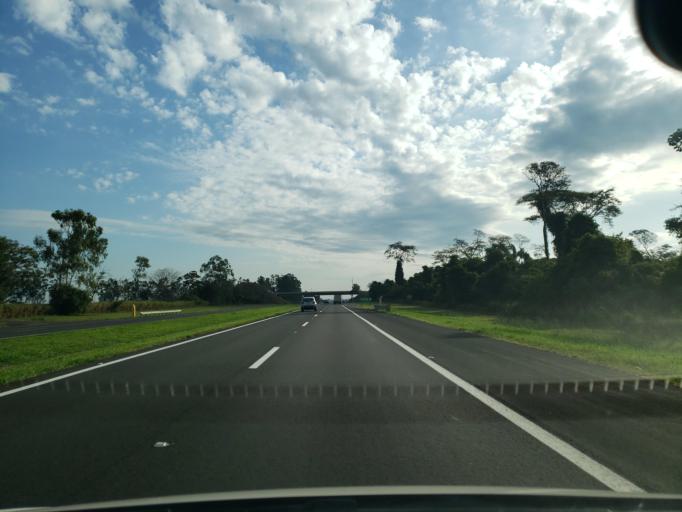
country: BR
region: Sao Paulo
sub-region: Guararapes
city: Guararapes
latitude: -21.2039
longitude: -50.6130
